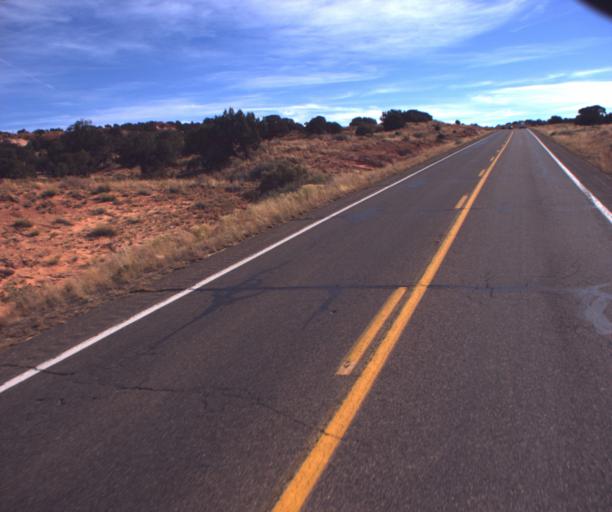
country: US
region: Arizona
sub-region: Coconino County
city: Kaibito
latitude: 36.5777
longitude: -111.1296
